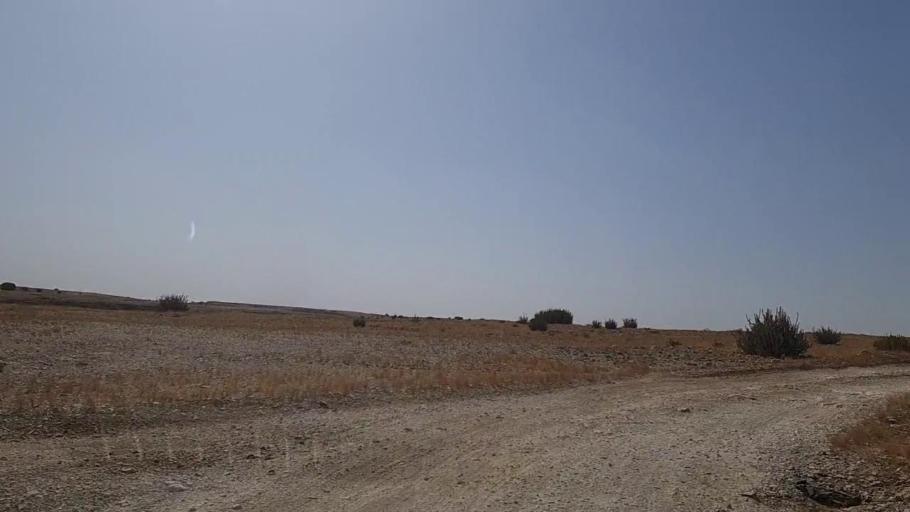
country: PK
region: Sindh
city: Kotri
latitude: 25.1640
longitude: 68.1906
